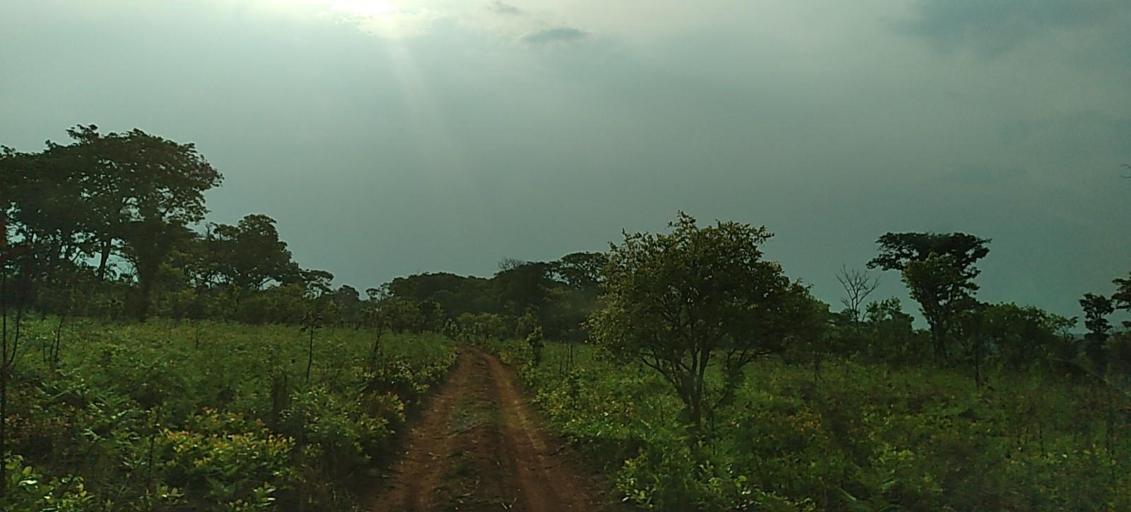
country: ZM
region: North-Western
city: Solwezi
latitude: -12.0430
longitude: 26.0495
